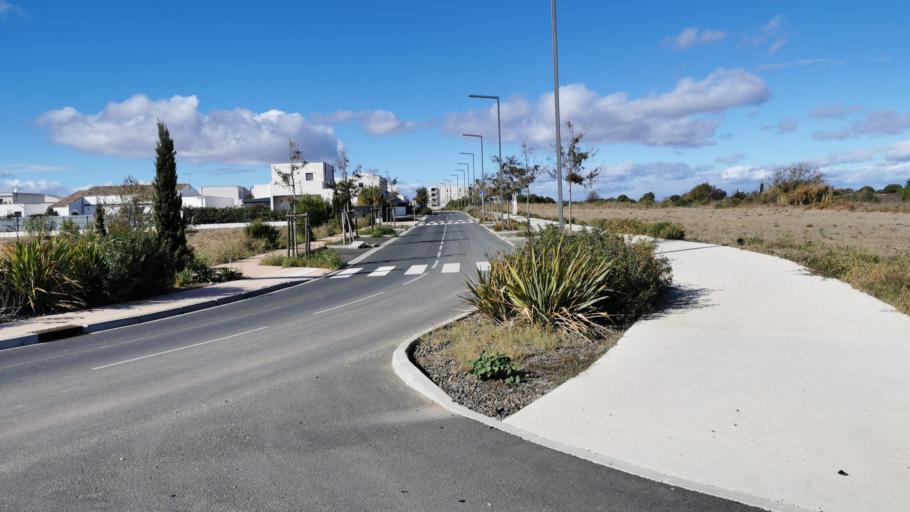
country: FR
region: Languedoc-Roussillon
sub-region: Departement de l'Herault
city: Valras-Plage
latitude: 43.2447
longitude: 3.2692
